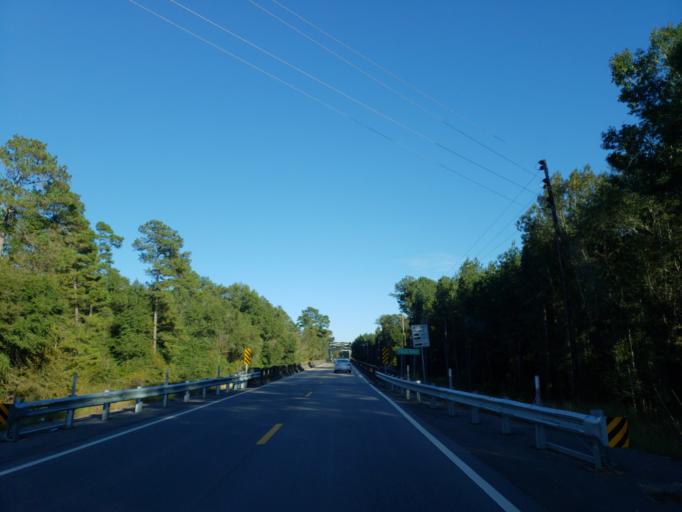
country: US
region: Mississippi
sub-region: Perry County
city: Richton
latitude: 31.3582
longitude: -89.0283
